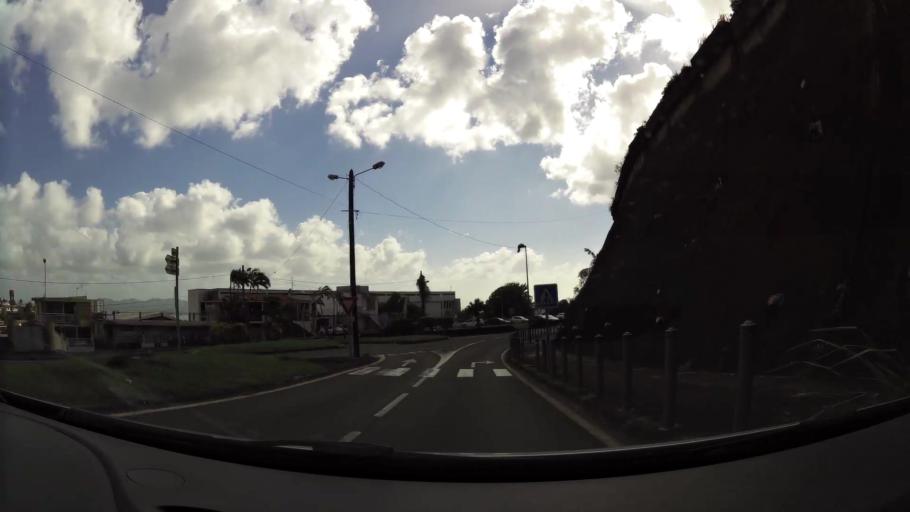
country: MQ
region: Martinique
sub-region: Martinique
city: Fort-de-France
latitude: 14.6154
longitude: -61.0620
